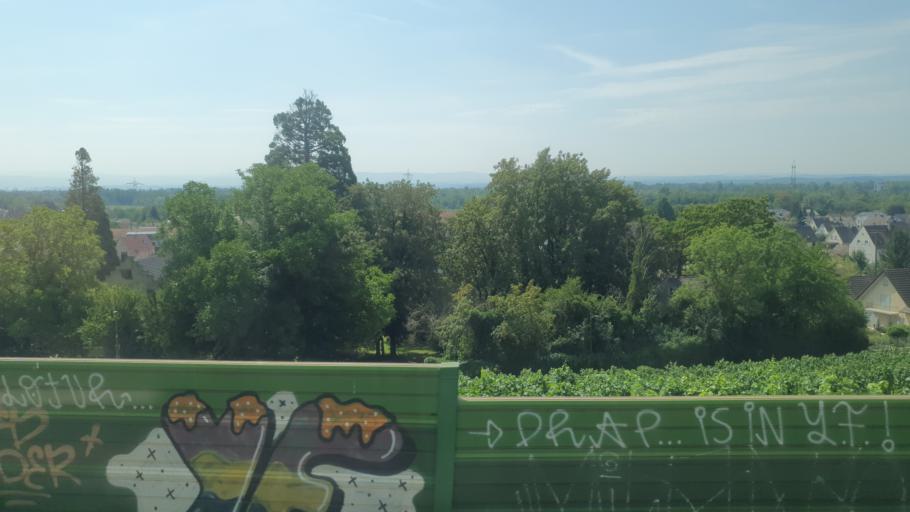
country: FR
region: Alsace
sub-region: Departement du Haut-Rhin
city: Rosenau
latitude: 47.6617
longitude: 7.5408
